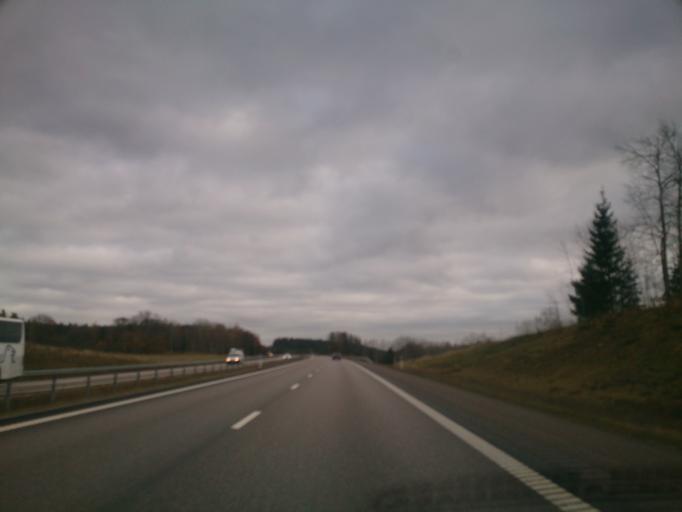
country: SE
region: OEstergoetland
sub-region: Norrkopings Kommun
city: Krokek
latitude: 58.7426
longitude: 16.4832
